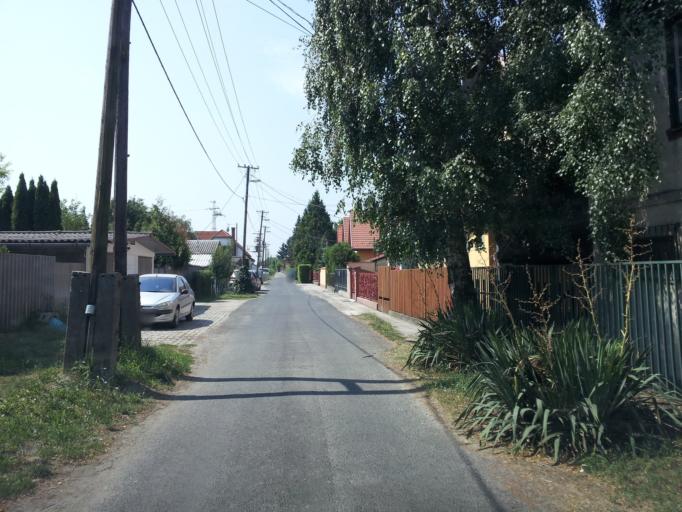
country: HU
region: Pest
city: Szigethalom
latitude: 47.2971
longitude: 19.0254
